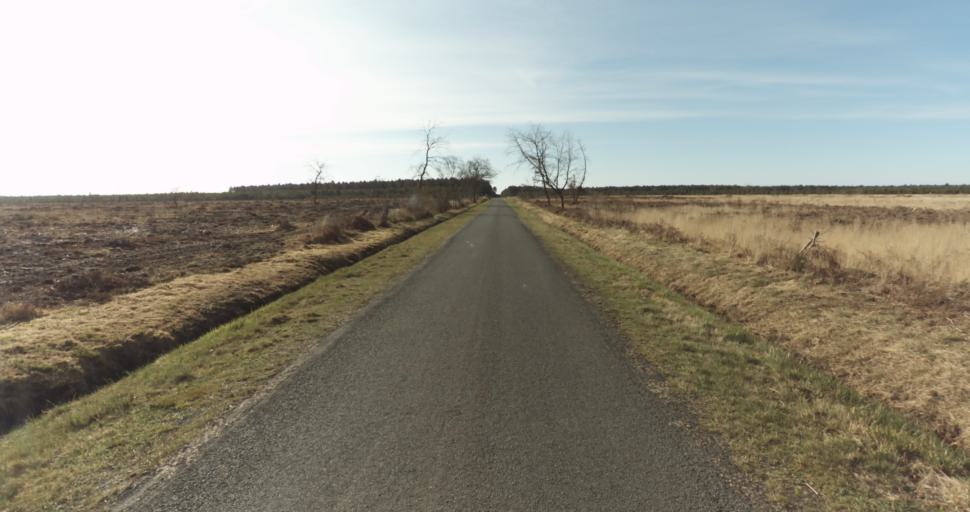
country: FR
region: Aquitaine
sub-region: Departement des Landes
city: Sarbazan
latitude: 44.0380
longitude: -0.2396
